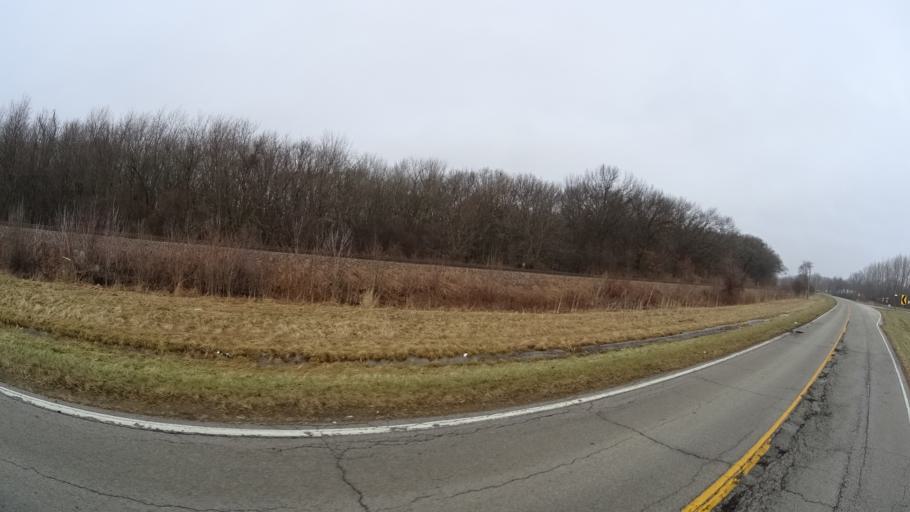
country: US
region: Illinois
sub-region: Cook County
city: Glenwood
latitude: 41.5373
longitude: -87.6127
